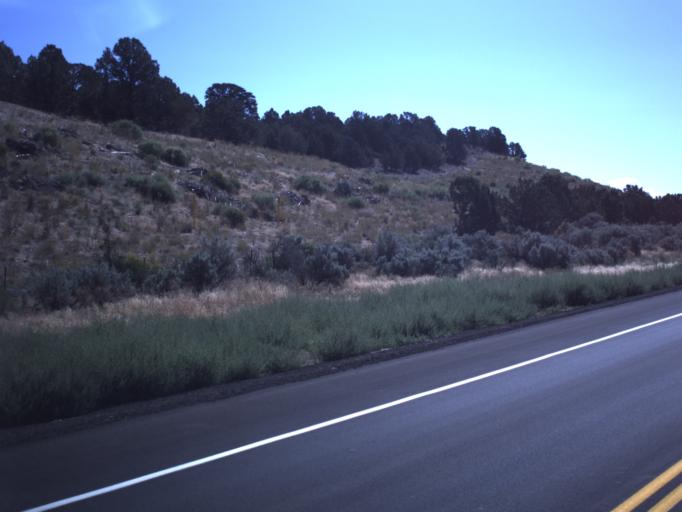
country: US
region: Utah
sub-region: Utah County
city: Genola
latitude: 39.9740
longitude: -112.2584
